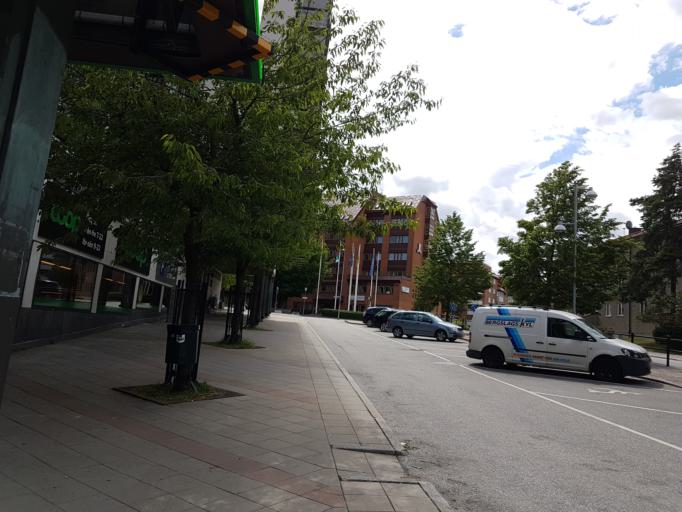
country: SE
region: Stockholm
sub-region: Lidingo
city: Lidingoe
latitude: 59.3631
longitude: 18.1232
